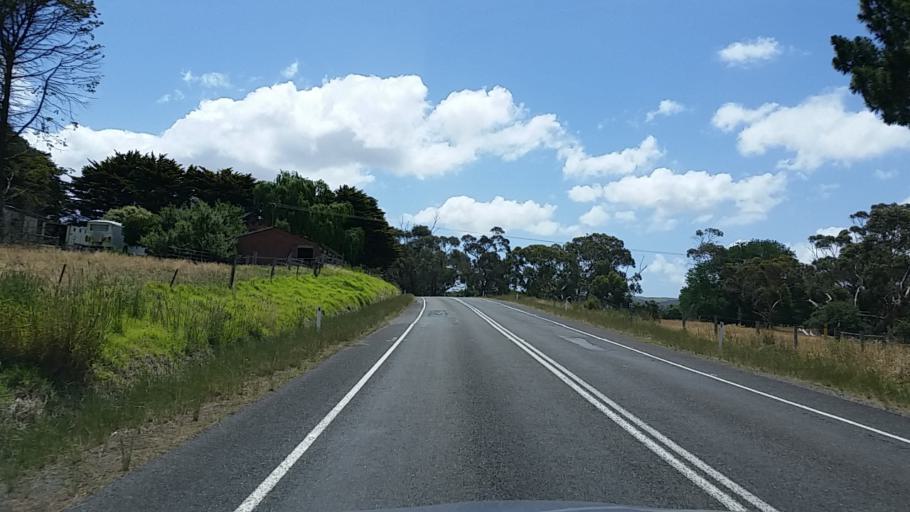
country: AU
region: South Australia
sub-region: Alexandrina
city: Mount Compass
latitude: -35.4376
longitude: 138.5942
